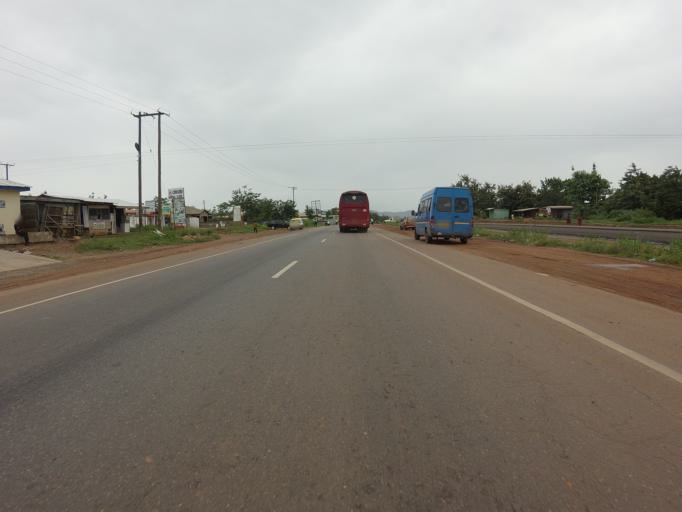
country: GH
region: Eastern
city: Suhum
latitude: 6.0527
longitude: -0.4630
